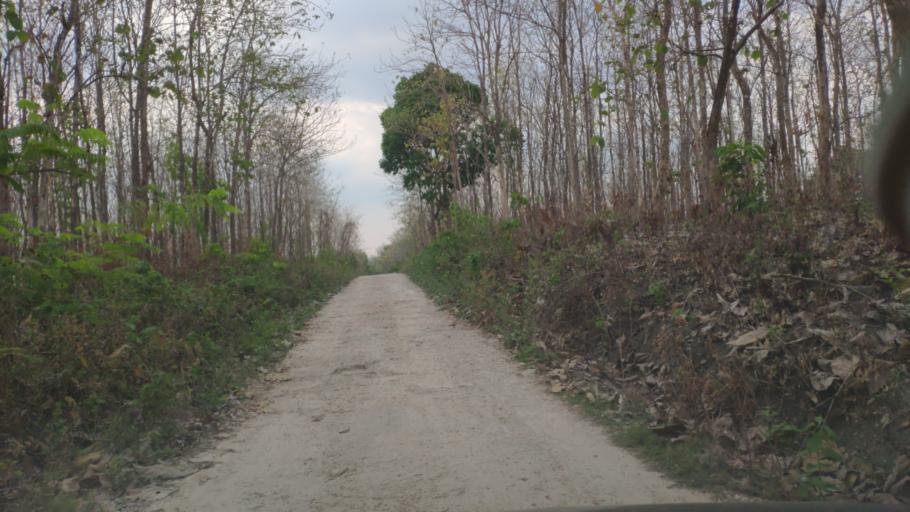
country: ID
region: Central Java
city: Randublatung
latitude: -7.2796
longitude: 111.2884
